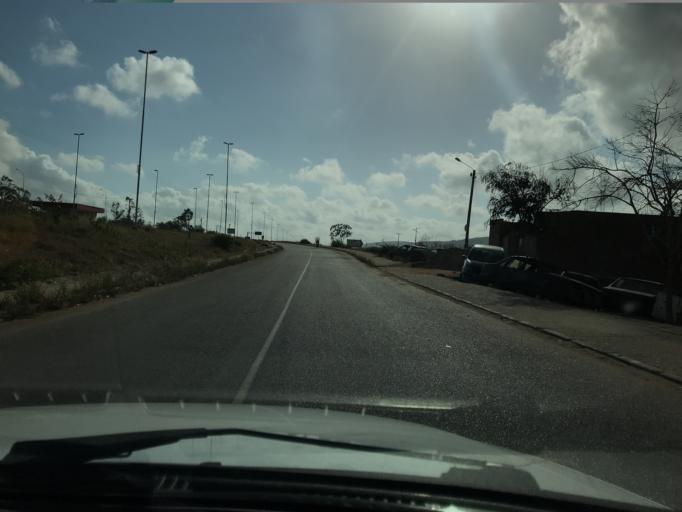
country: BR
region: Pernambuco
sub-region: Bezerros
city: Bezerros
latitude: -8.2371
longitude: -35.7338
